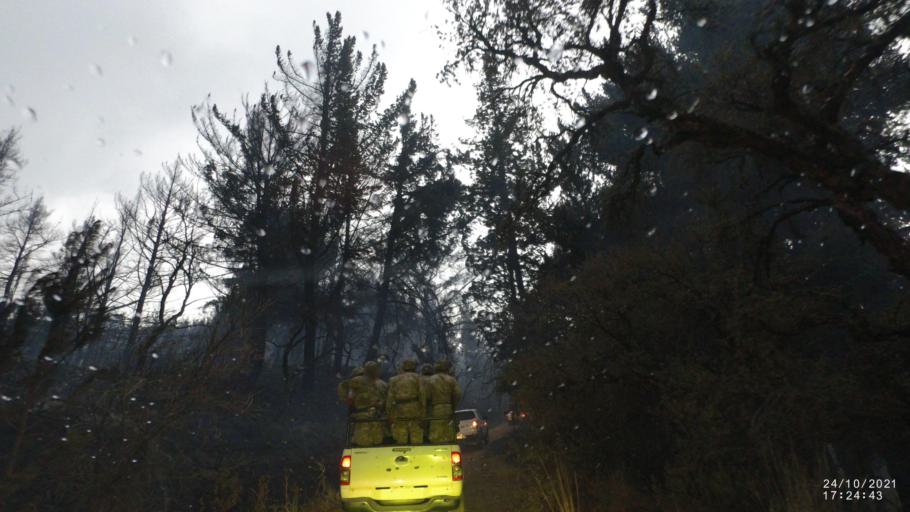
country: BO
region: Cochabamba
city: Cochabamba
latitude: -17.3258
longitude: -66.1346
